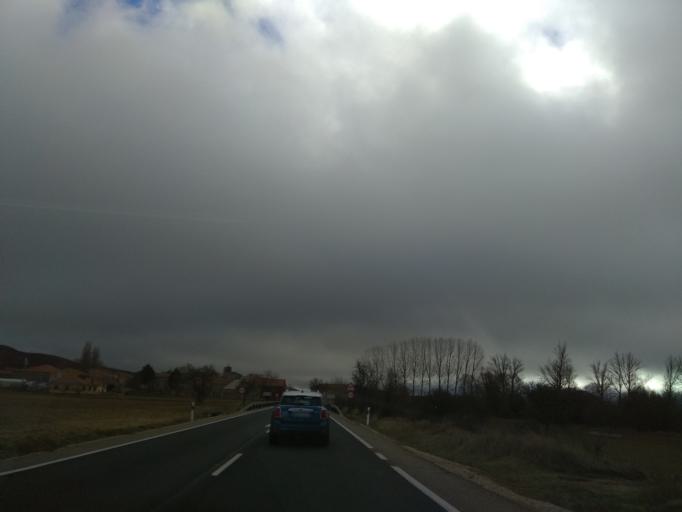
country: ES
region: Castille and Leon
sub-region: Provincia de Burgos
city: Tubilla del Agua
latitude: 42.6474
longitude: -3.8865
